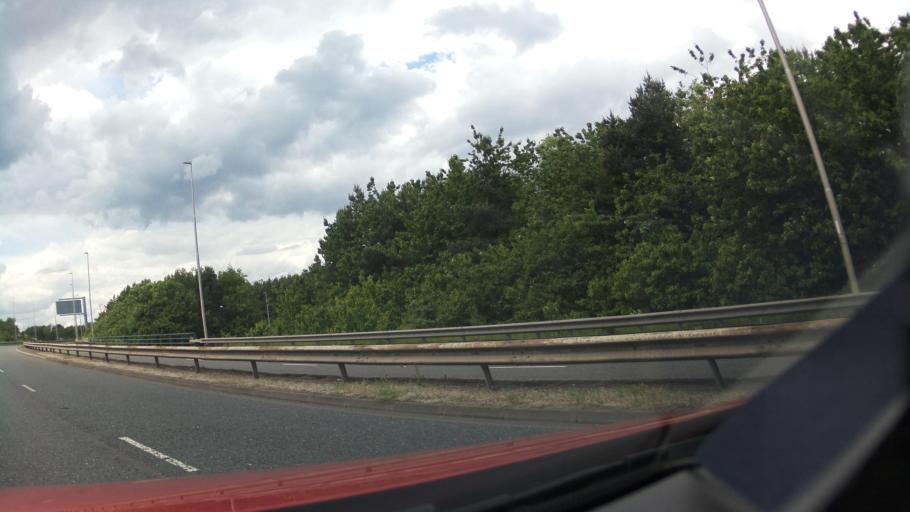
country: GB
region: England
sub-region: Sunderland
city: Washington
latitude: 54.9012
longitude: -1.5469
